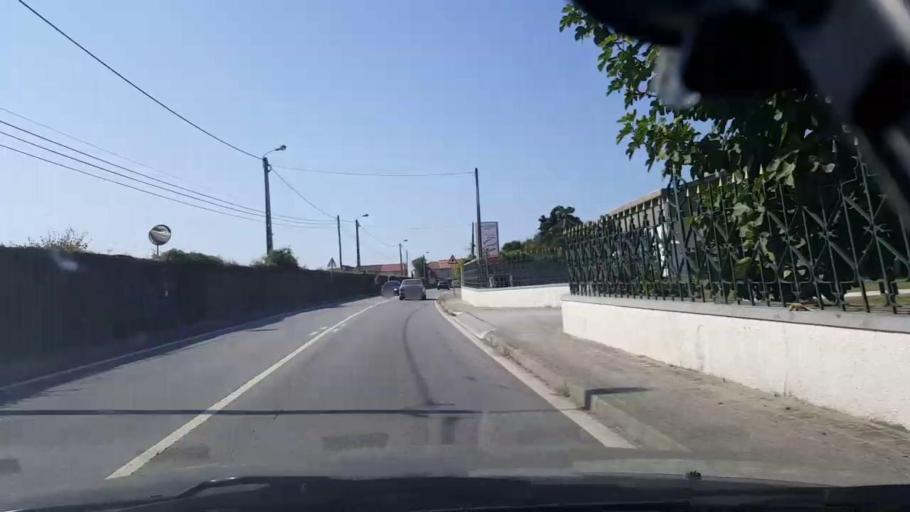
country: PT
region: Porto
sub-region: Povoa de Varzim
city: Pedroso
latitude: 41.3947
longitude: -8.6900
